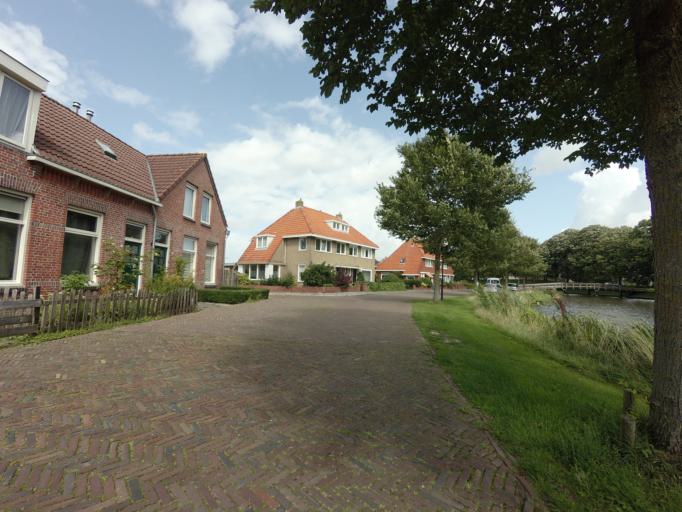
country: NL
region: Friesland
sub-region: Gemeente Franekeradeel
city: Franeker
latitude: 53.1872
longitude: 5.5368
